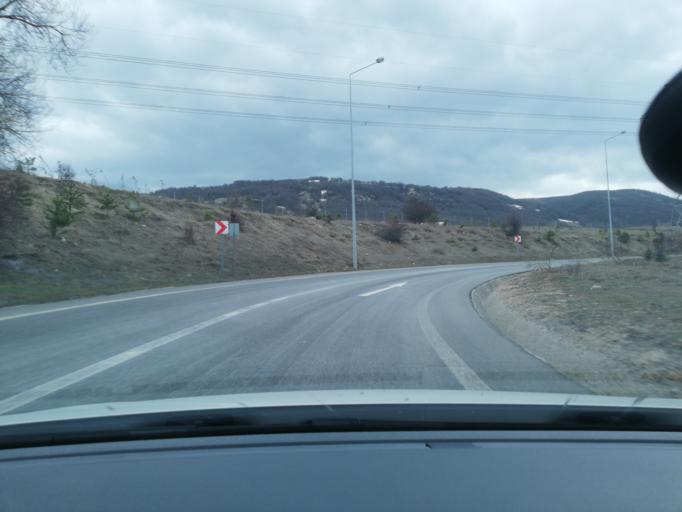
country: TR
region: Bolu
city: Yenicaga
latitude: 40.7629
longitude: 32.0100
